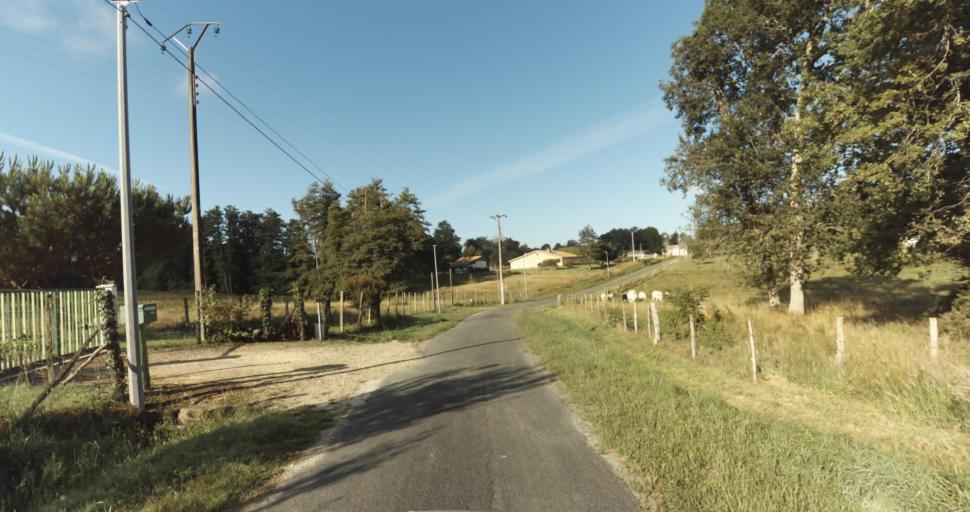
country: FR
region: Aquitaine
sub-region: Departement de la Gironde
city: Bazas
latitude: 44.4475
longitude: -0.2565
